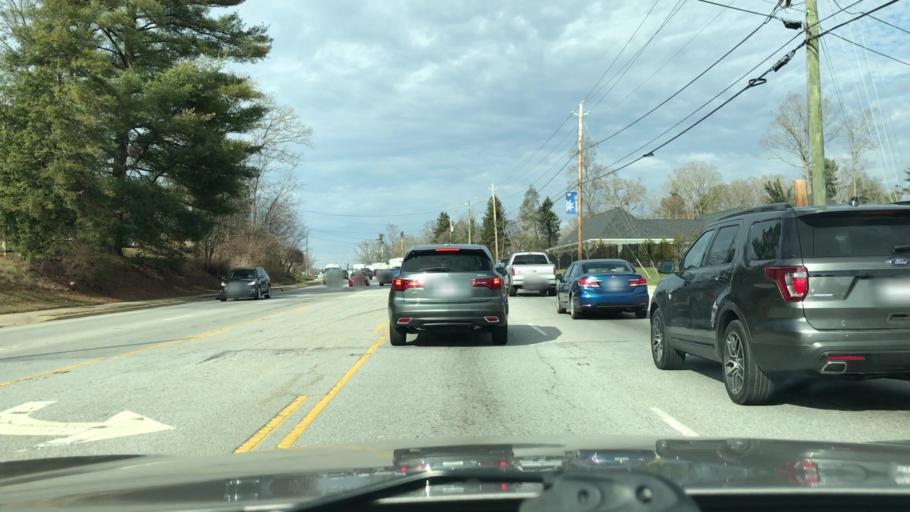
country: US
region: North Carolina
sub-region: Henderson County
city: Fletcher
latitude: 35.4375
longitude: -82.5029
